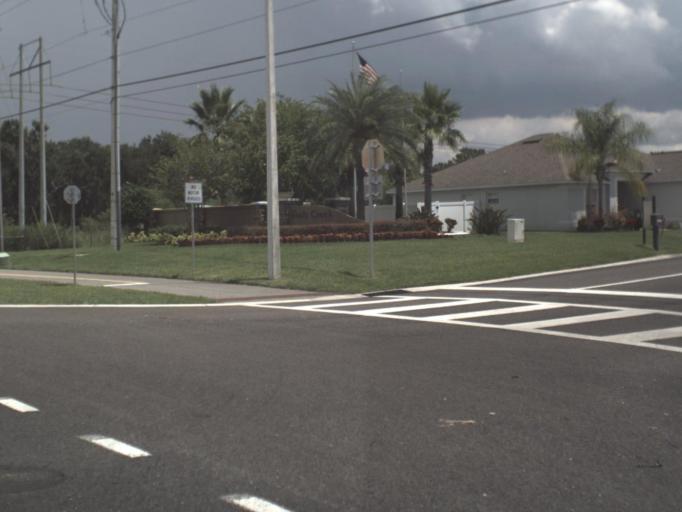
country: US
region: Florida
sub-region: Hillsborough County
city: Sun City Center
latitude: 27.7764
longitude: -82.3348
